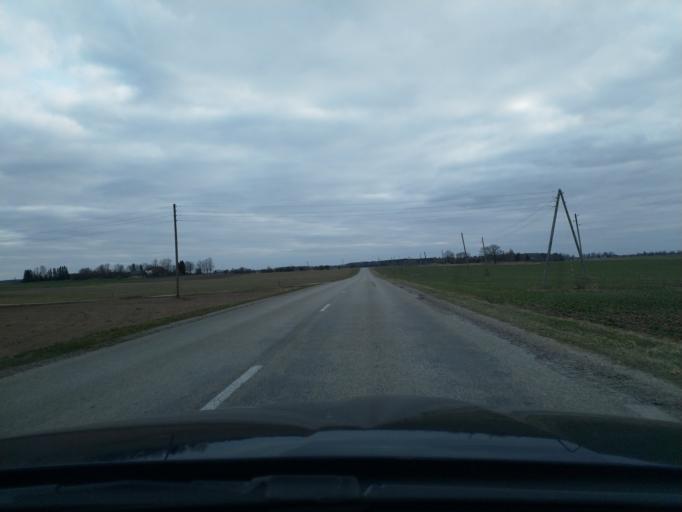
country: LV
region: Talsu Rajons
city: Sabile
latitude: 56.9503
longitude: 22.6063
